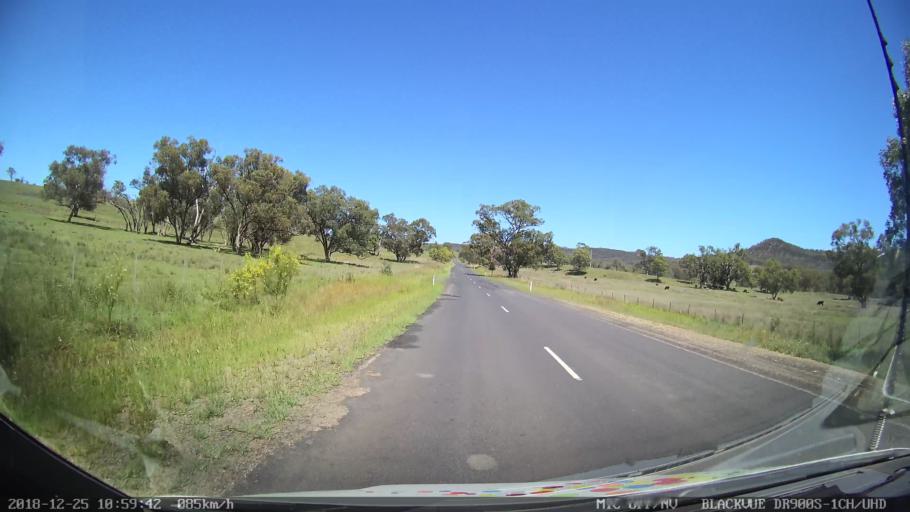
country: AU
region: New South Wales
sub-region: Upper Hunter Shire
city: Merriwa
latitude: -32.4021
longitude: 150.2195
